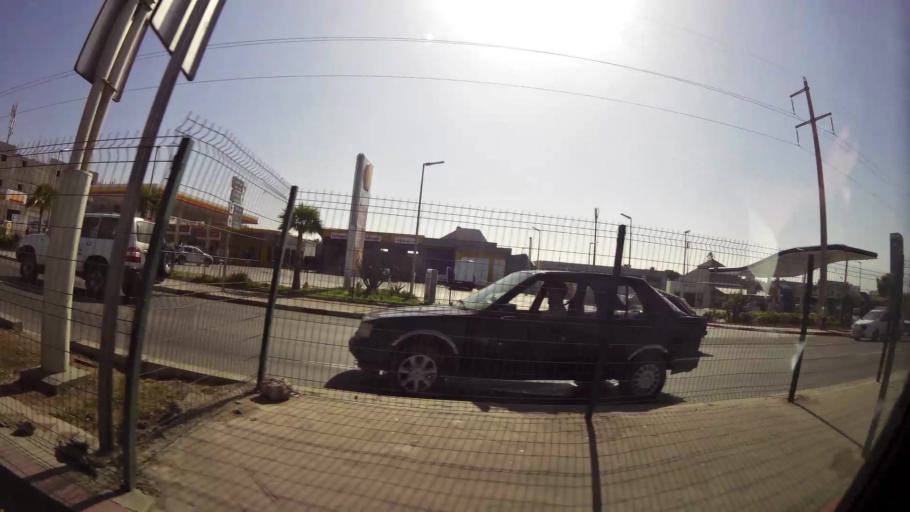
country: MA
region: Souss-Massa-Draa
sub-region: Inezgane-Ait Mellou
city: Inezgane
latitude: 30.3781
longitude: -9.5047
